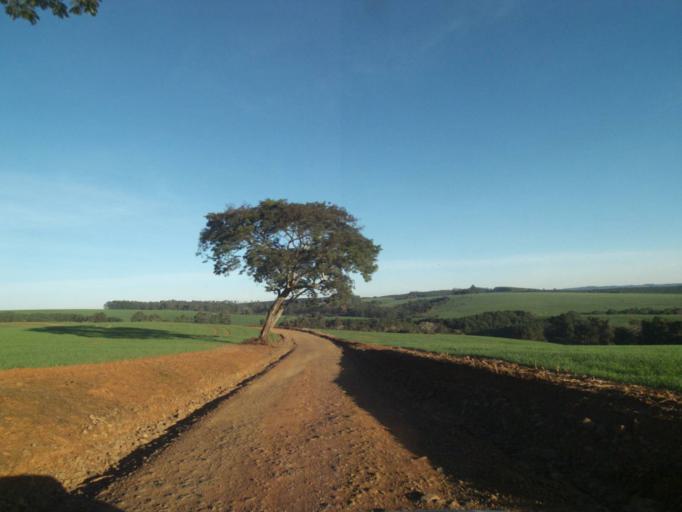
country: BR
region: Parana
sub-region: Telemaco Borba
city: Telemaco Borba
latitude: -24.4675
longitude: -50.5959
